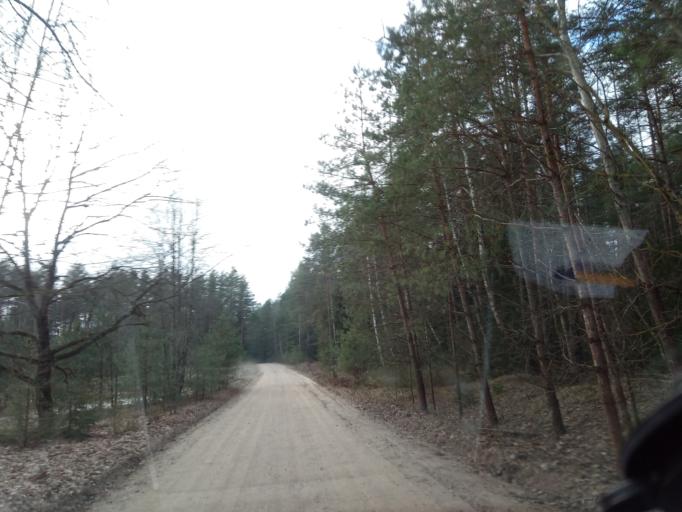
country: LT
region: Alytaus apskritis
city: Druskininkai
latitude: 53.9640
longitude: 24.3092
